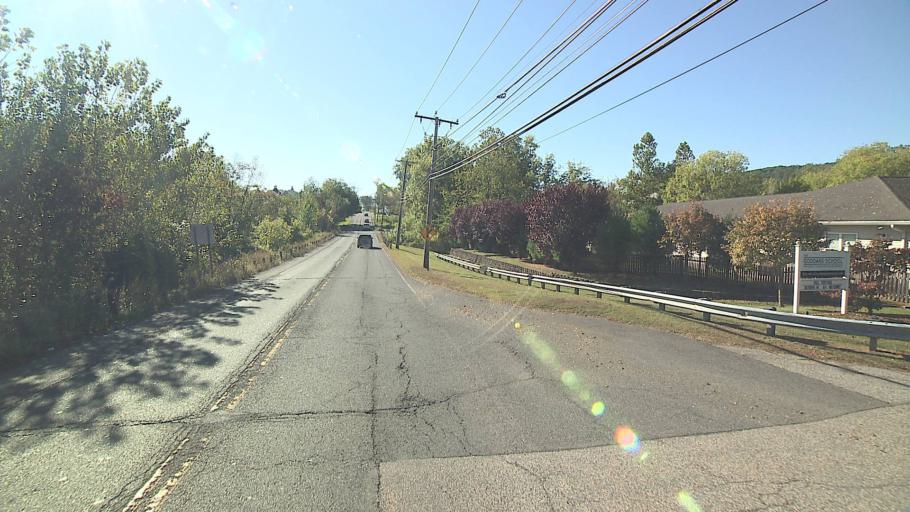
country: US
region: Connecticut
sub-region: Litchfield County
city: New Milford
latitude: 41.4928
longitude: -73.4160
